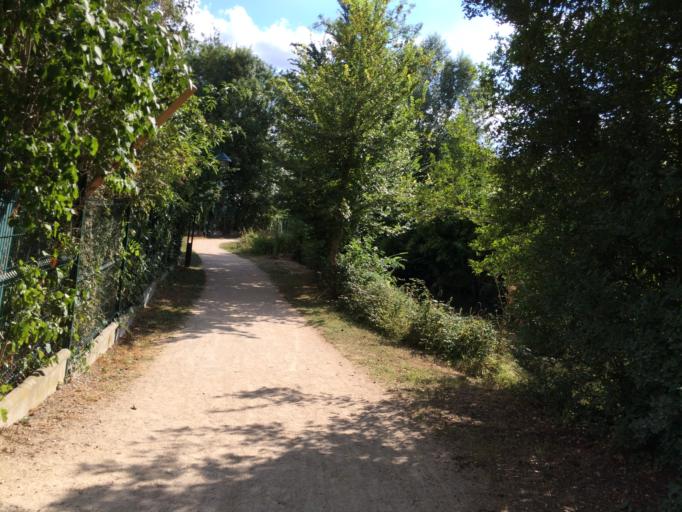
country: FR
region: Ile-de-France
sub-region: Departement de l'Essonne
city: Villebon-sur-Yvette
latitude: 48.7042
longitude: 2.2426
